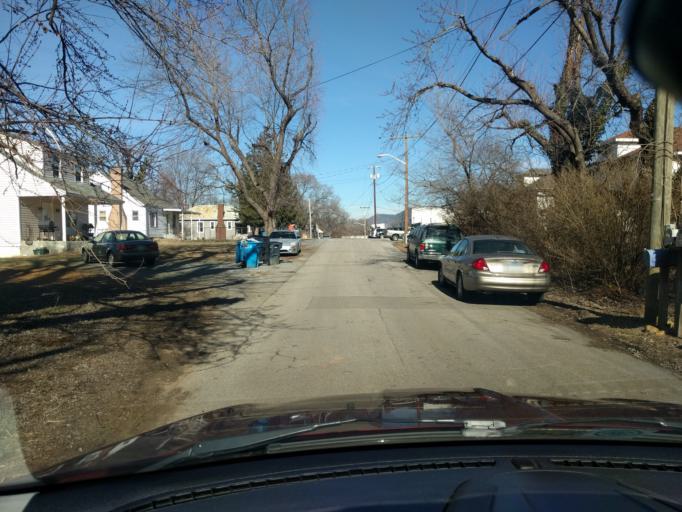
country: US
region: Virginia
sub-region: City of Roanoke
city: Roanoke
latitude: 37.3040
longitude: -79.9301
